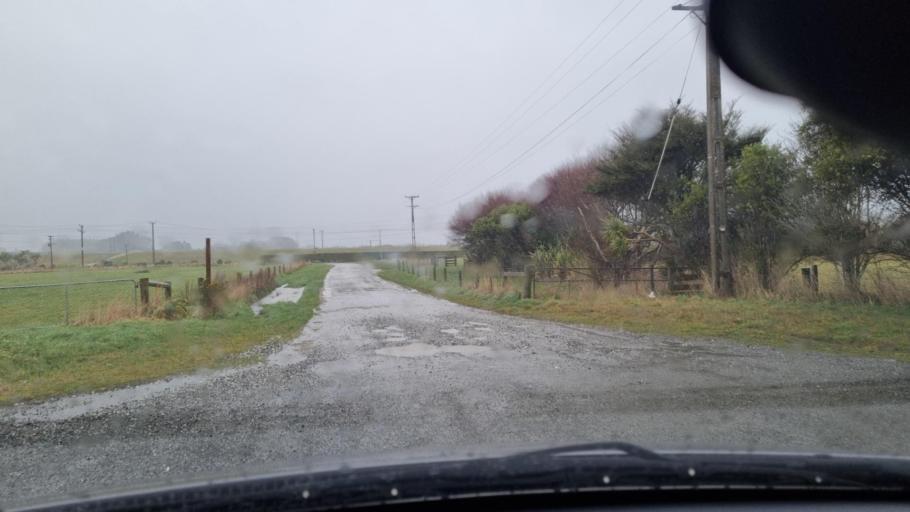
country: NZ
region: Southland
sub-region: Invercargill City
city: Invercargill
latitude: -46.3854
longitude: 168.3916
